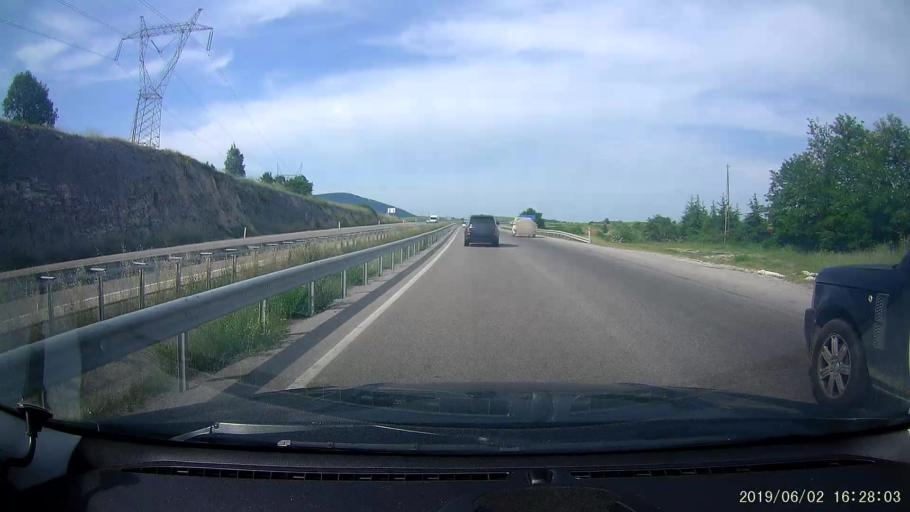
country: TR
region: Samsun
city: Ladik
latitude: 41.0046
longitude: 35.8399
